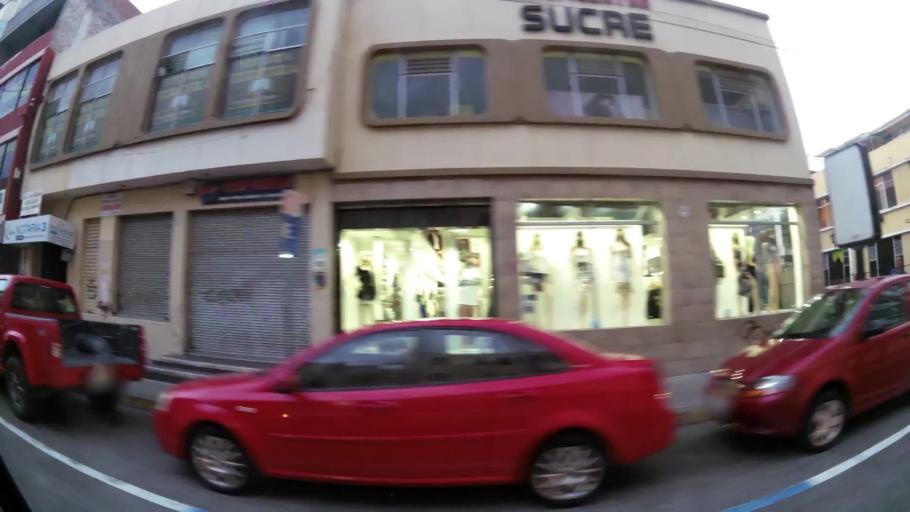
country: EC
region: Tungurahua
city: Ambato
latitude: -1.2434
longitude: -78.6302
